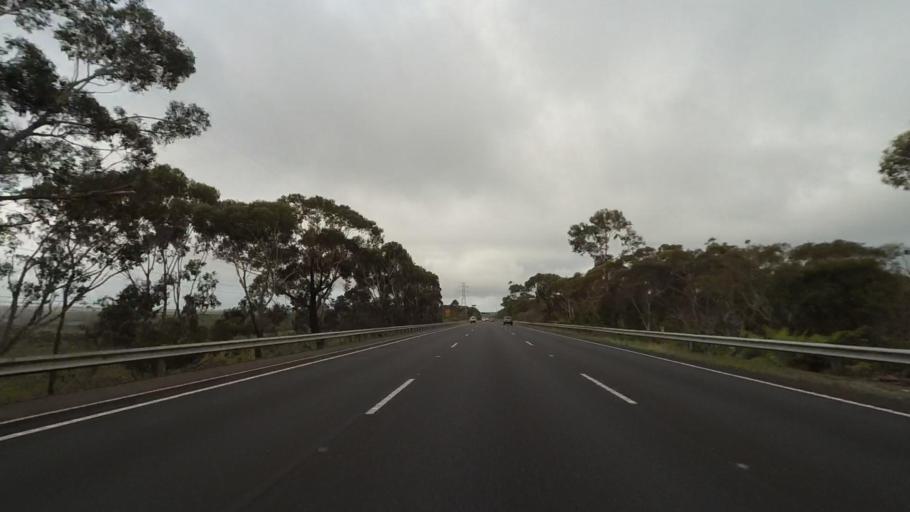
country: AU
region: New South Wales
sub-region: Wollongong
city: Bulli
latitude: -34.2954
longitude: 150.9170
